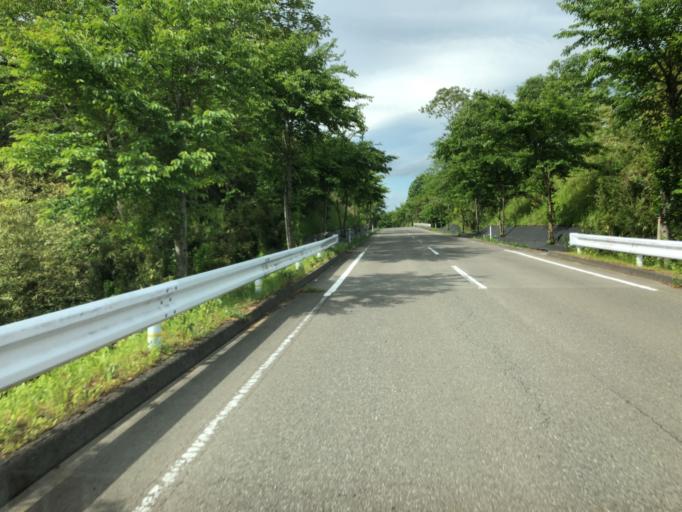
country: JP
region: Fukushima
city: Nihommatsu
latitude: 37.6278
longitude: 140.5209
